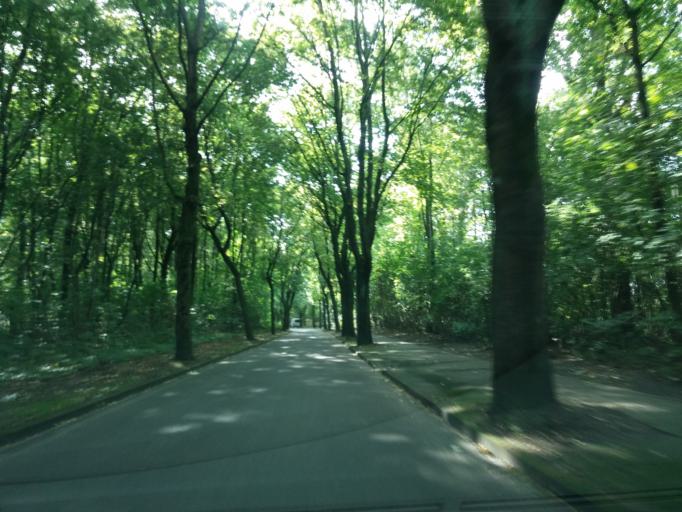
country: DE
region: North Rhine-Westphalia
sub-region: Regierungsbezirk Munster
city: Gladbeck
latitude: 51.5957
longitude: 7.0144
